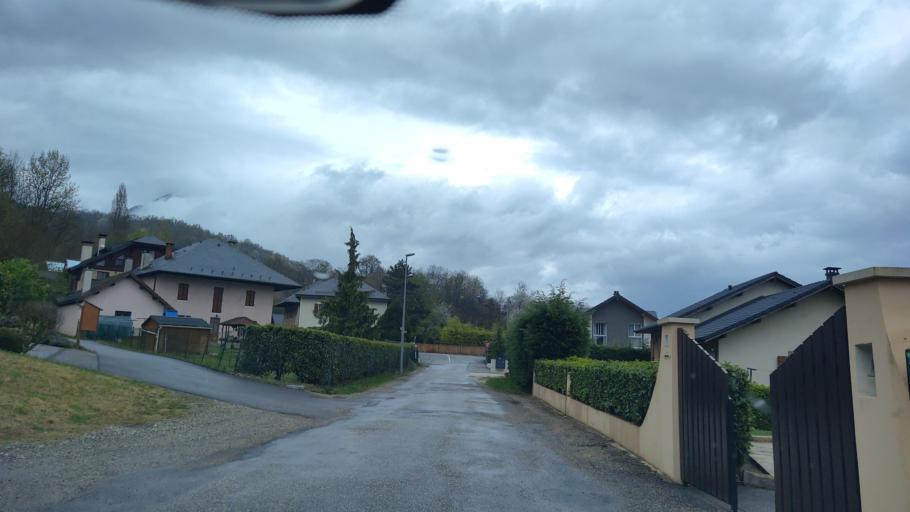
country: FR
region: Rhone-Alpes
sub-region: Departement de la Savoie
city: Frontenex
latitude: 45.6381
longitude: 6.3048
